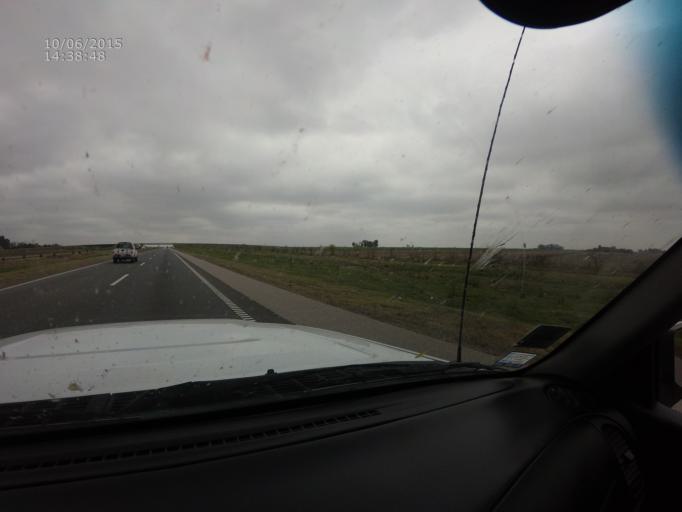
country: AR
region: Cordoba
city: James Craik
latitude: -32.0870
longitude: -63.4788
